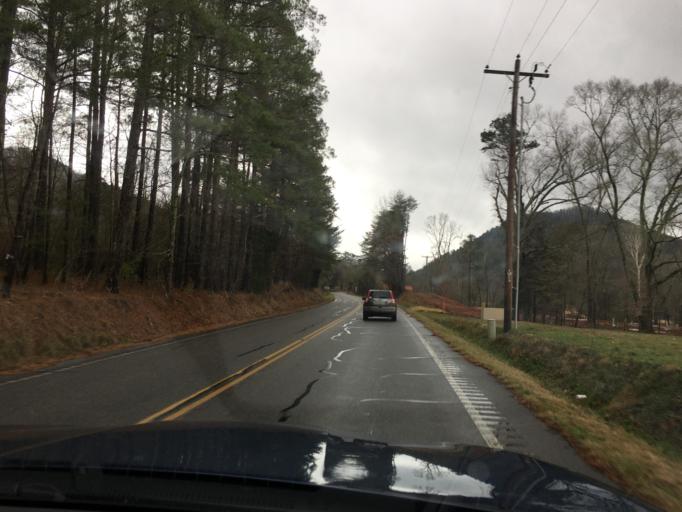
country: US
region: Tennessee
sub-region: Polk County
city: Benton
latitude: 35.1041
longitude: -84.6544
